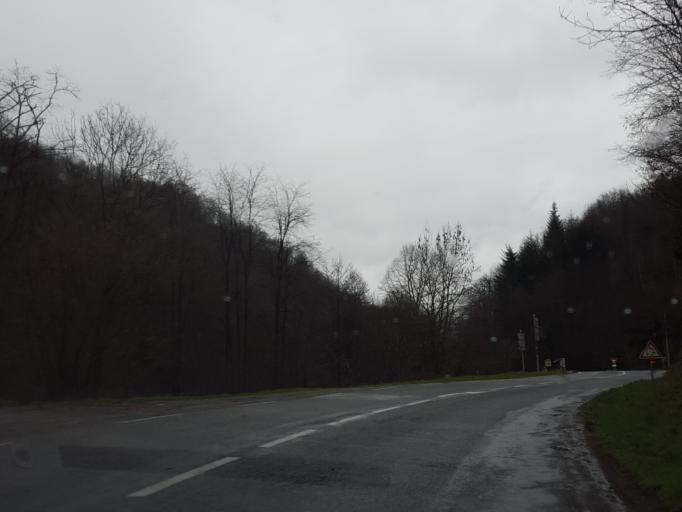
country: FR
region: Midi-Pyrenees
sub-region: Departement de l'Ariege
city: Saint-Girons
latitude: 42.9101
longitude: 1.2130
